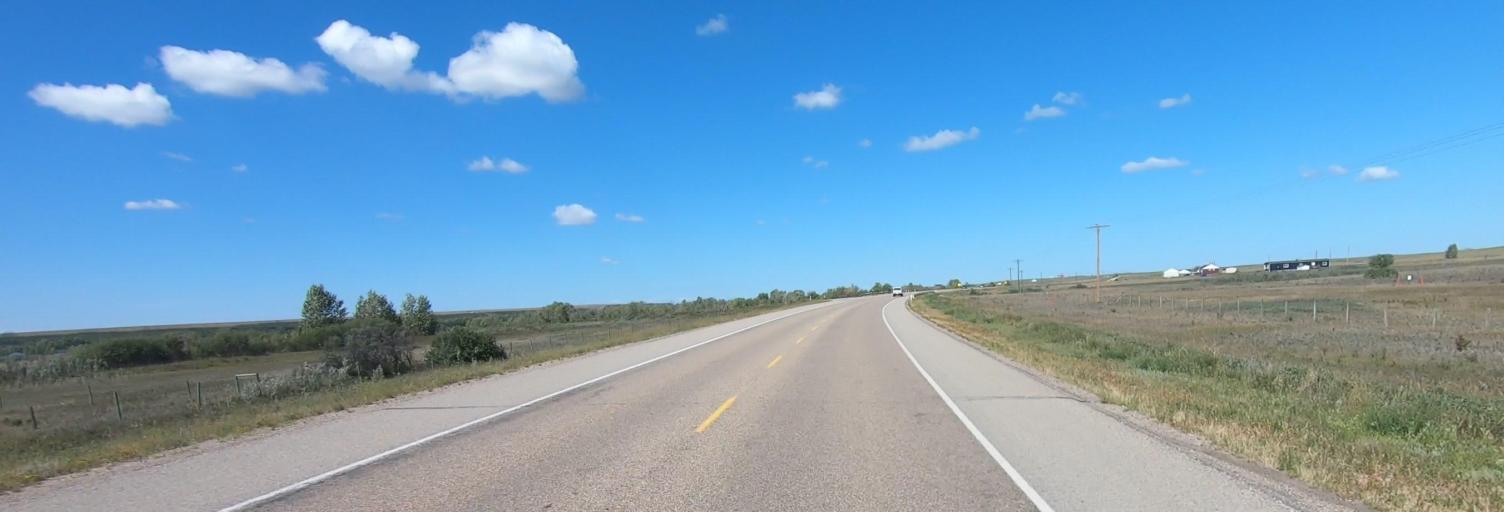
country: CA
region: Alberta
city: Strathmore
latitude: 50.8558
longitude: -113.1306
